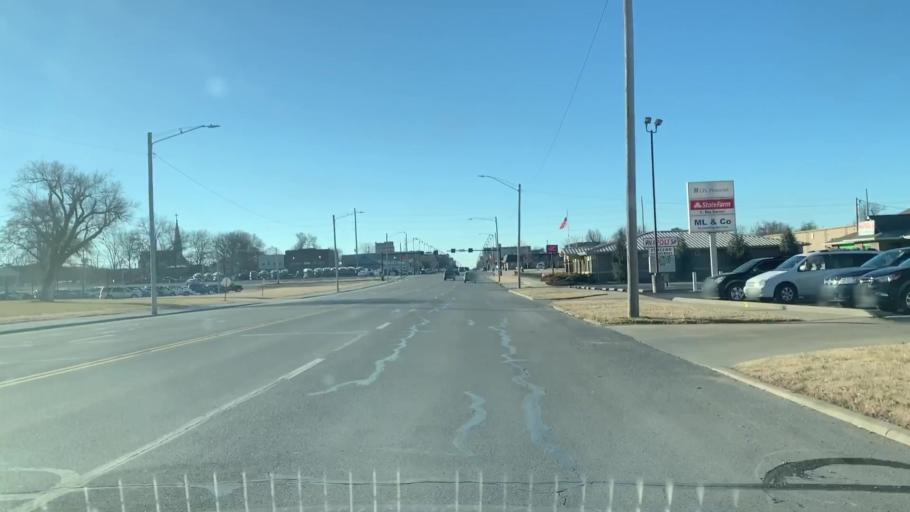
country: US
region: Kansas
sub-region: Crawford County
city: Pittsburg
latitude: 37.4201
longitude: -94.7050
